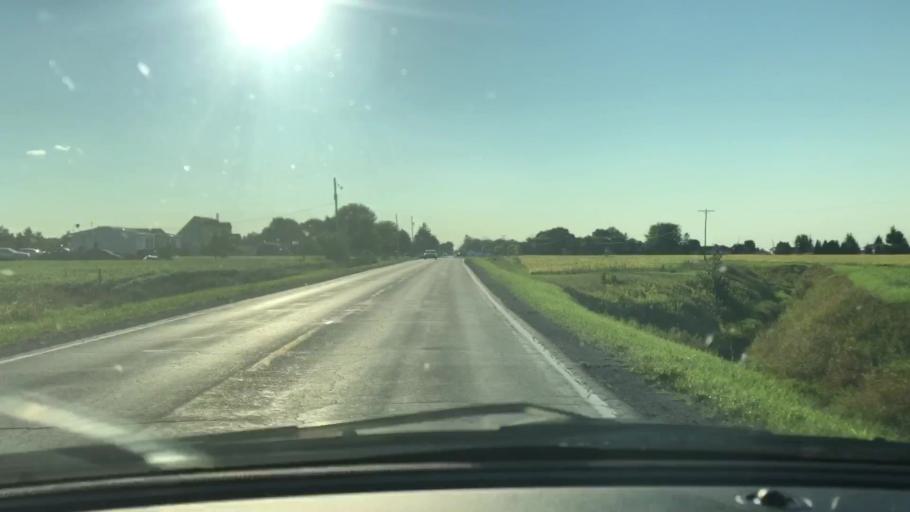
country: US
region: Michigan
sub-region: Bay County
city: Auburn
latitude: 43.6396
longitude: -84.0787
